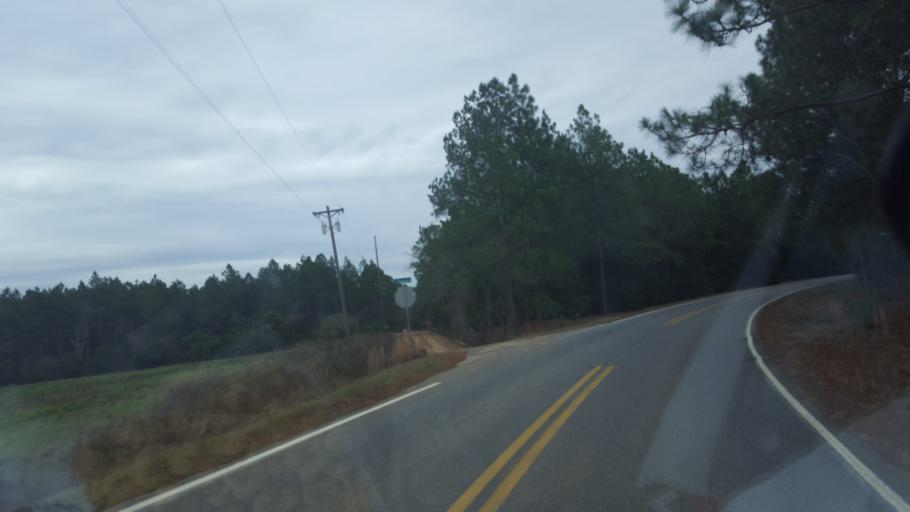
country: US
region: Georgia
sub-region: Ben Hill County
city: Fitzgerald
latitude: 31.7703
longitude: -83.3564
